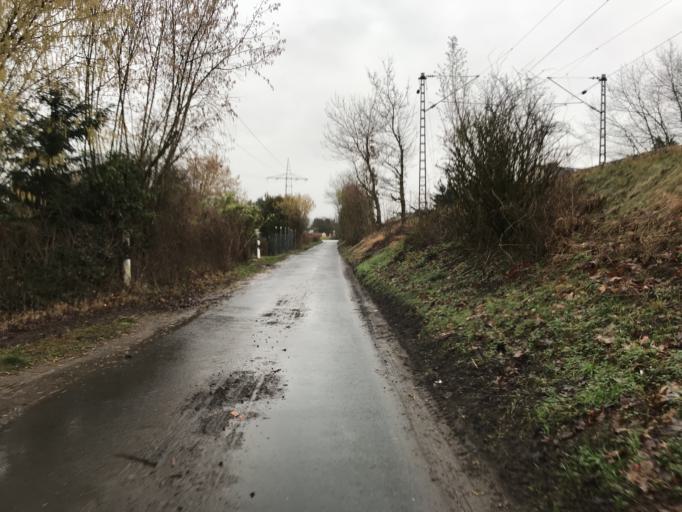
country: DE
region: Rheinland-Pfalz
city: Budenheim
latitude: 50.0205
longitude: 8.1599
